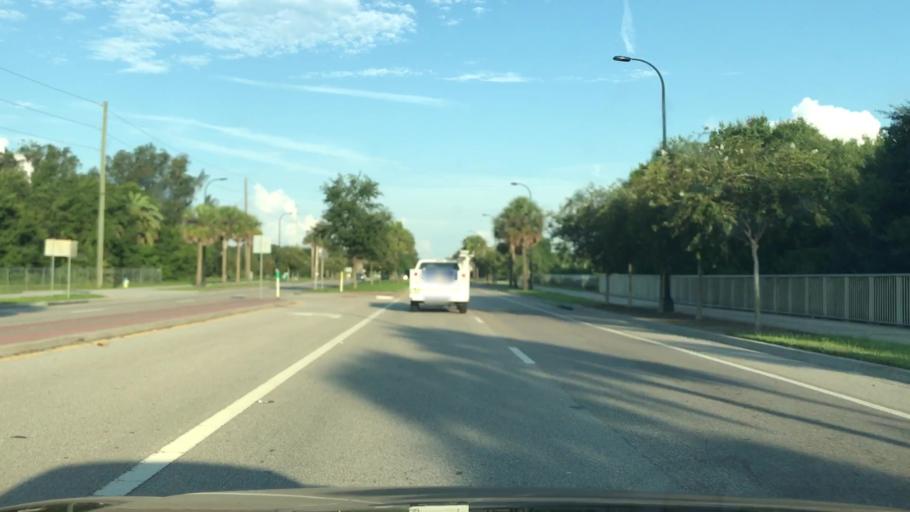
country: US
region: Florida
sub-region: Sarasota County
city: Fruitville
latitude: 27.3383
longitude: -82.4092
